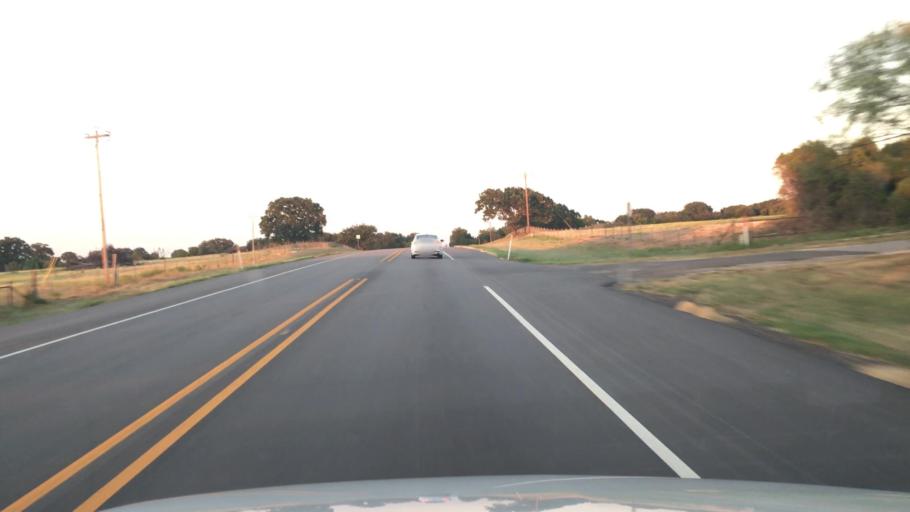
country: US
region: Texas
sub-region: Somervell County
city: Glen Rose
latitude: 32.1885
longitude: -97.8607
